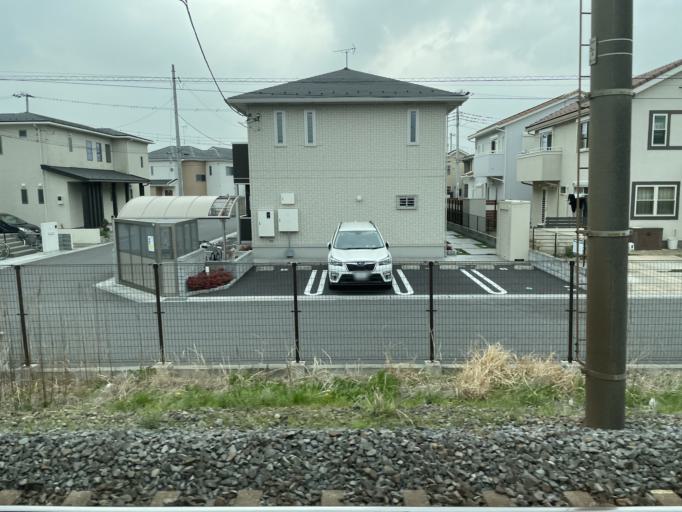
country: JP
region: Saitama
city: Sugito
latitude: 36.0142
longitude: 139.7350
